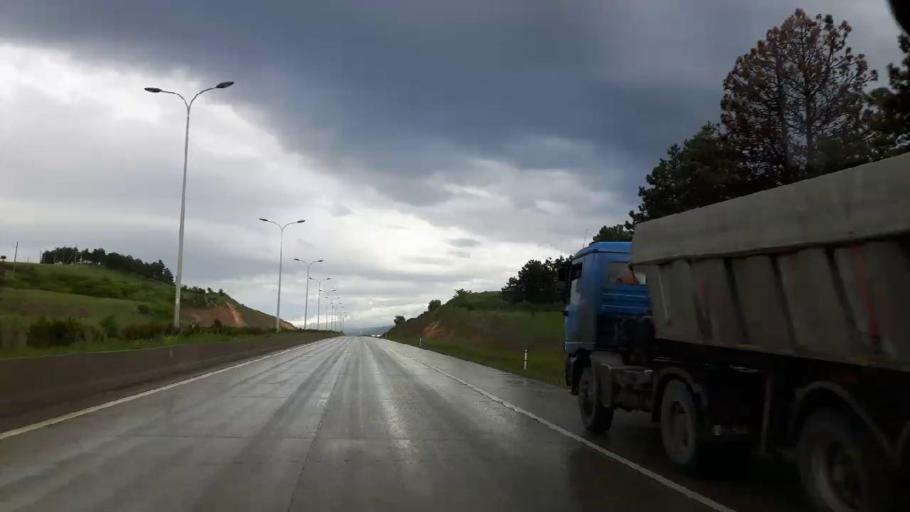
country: GE
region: Shida Kartli
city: Gori
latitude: 42.0098
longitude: 44.0429
